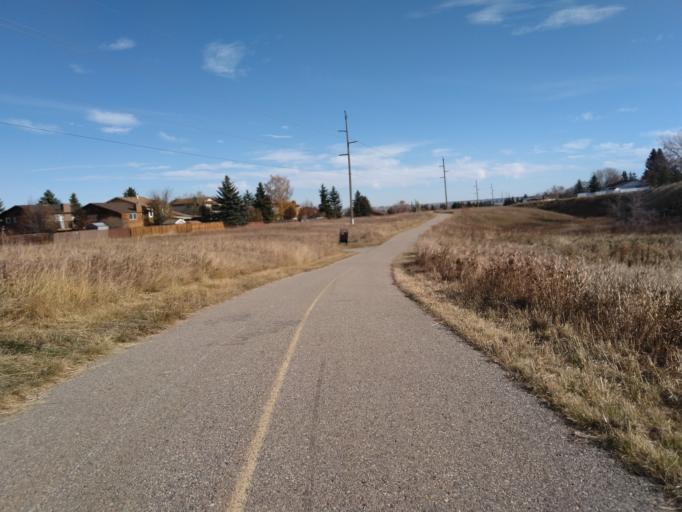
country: CA
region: Alberta
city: Calgary
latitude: 51.1246
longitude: -114.0924
